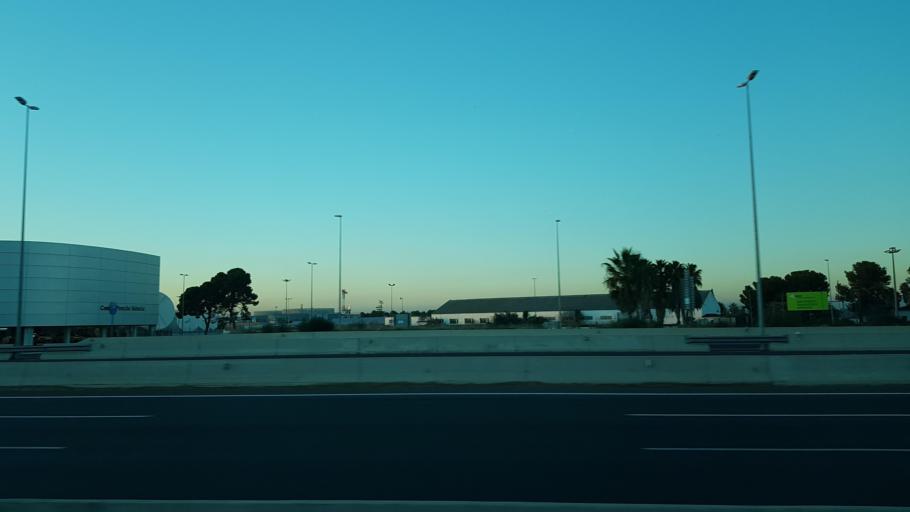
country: ES
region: Valencia
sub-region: Provincia de Valencia
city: Manises
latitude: 39.4760
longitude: -0.4833
